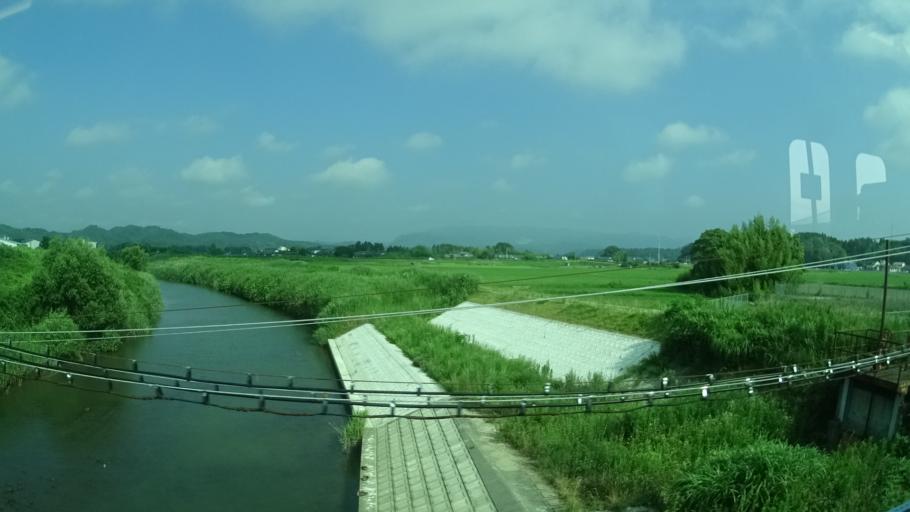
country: JP
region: Fukushima
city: Iwaki
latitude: 37.0949
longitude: 140.9728
